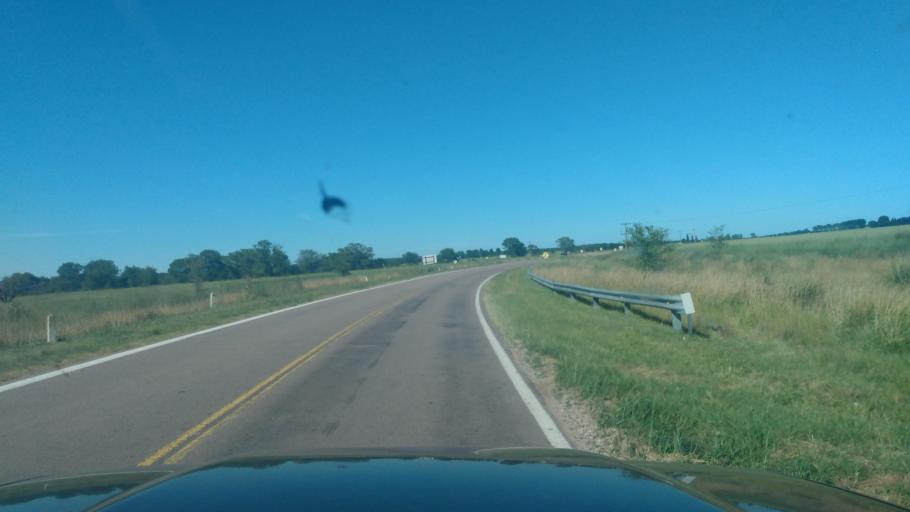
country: AR
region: La Pampa
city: General Acha
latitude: -37.3121
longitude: -64.2903
